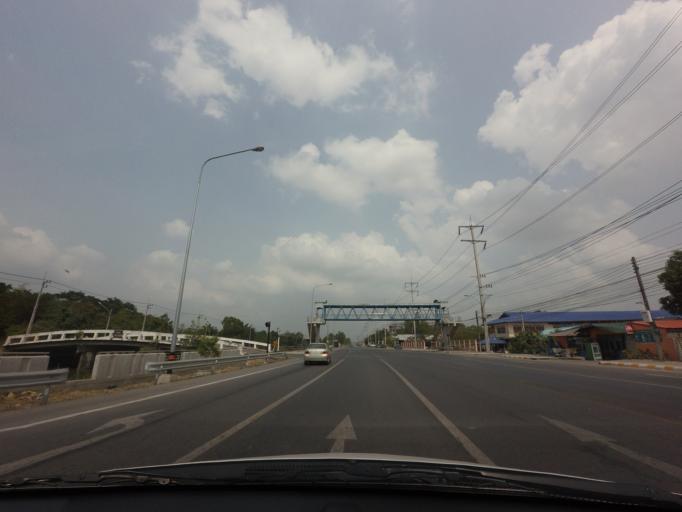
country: TH
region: Pathum Thani
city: Thanyaburi
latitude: 14.0587
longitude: 100.7102
